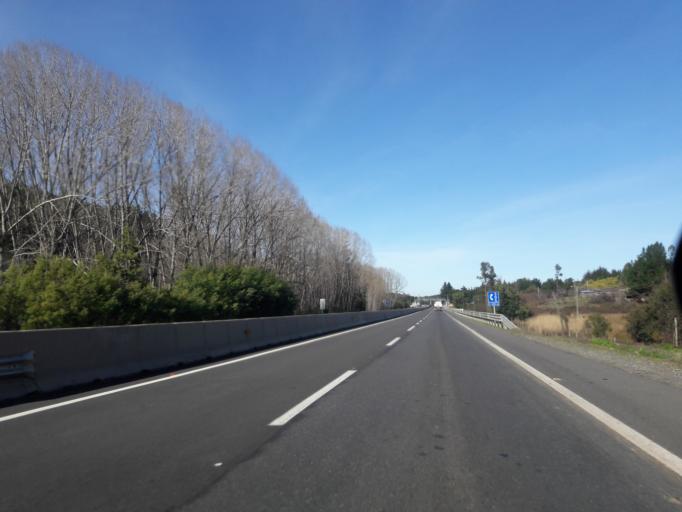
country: CL
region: Biobio
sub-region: Provincia de Biobio
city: Yumbel
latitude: -36.9460
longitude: -72.7530
